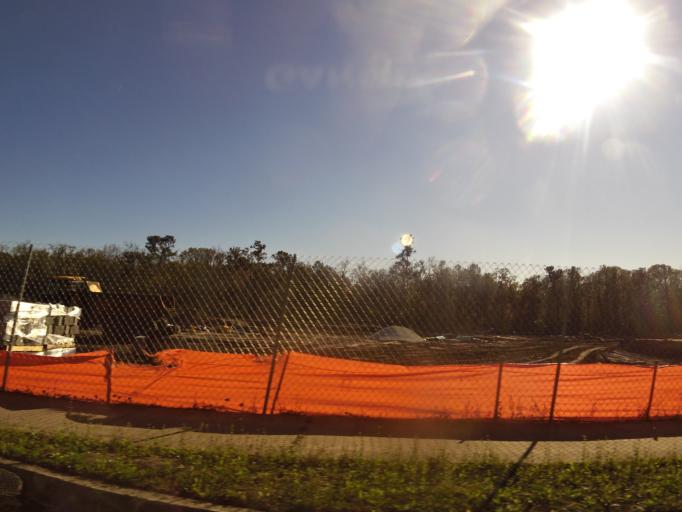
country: US
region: Florida
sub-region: Duval County
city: Jacksonville
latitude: 30.2478
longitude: -81.5701
